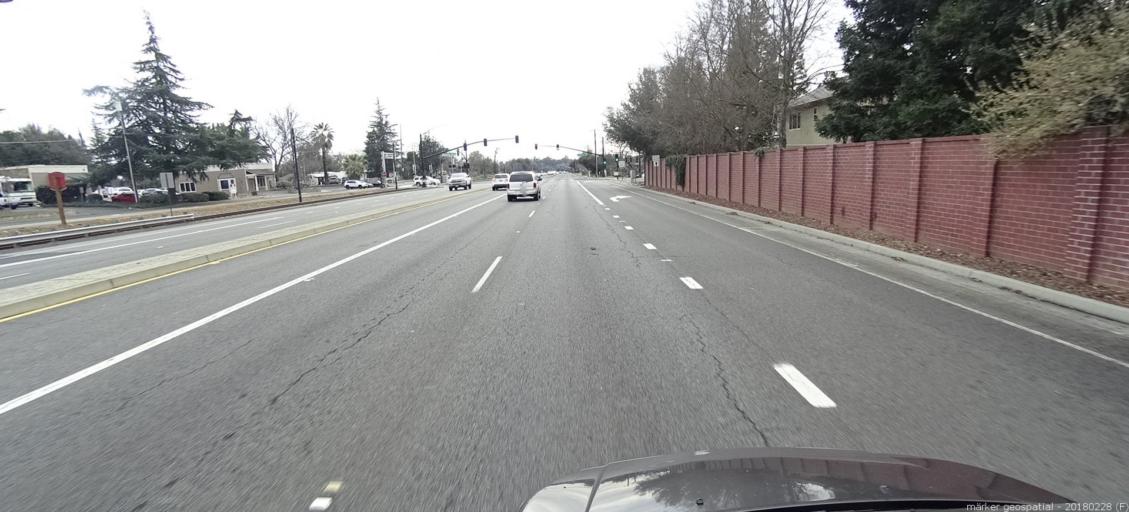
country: US
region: California
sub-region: Sacramento County
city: Folsom
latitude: 38.6728
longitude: -121.1816
